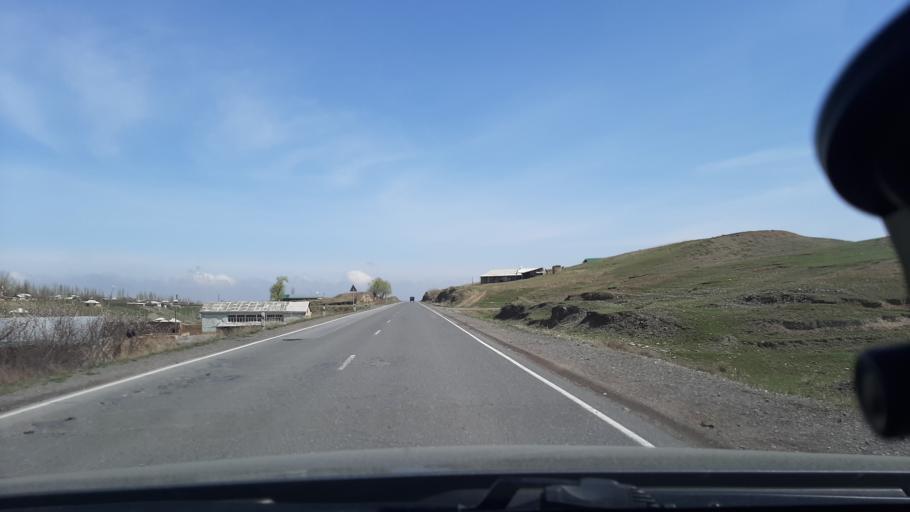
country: TJ
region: Viloyati Sughd
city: Shahriston
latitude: 39.7651
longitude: 68.8185
